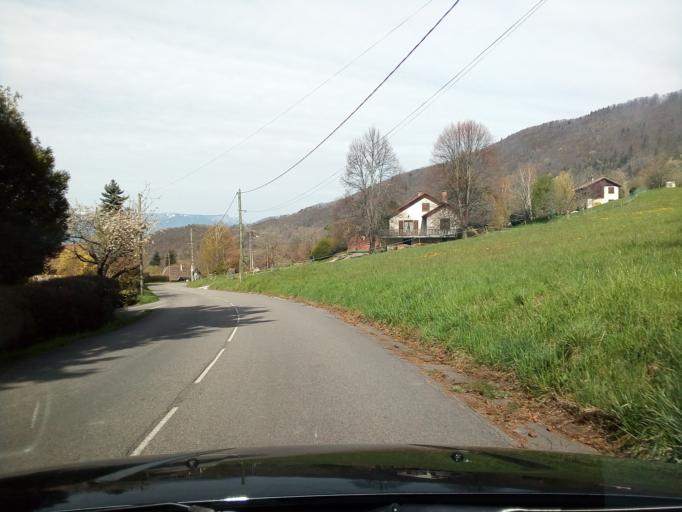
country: FR
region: Rhone-Alpes
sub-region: Departement de l'Isere
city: Revel
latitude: 45.1624
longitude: 5.8415
